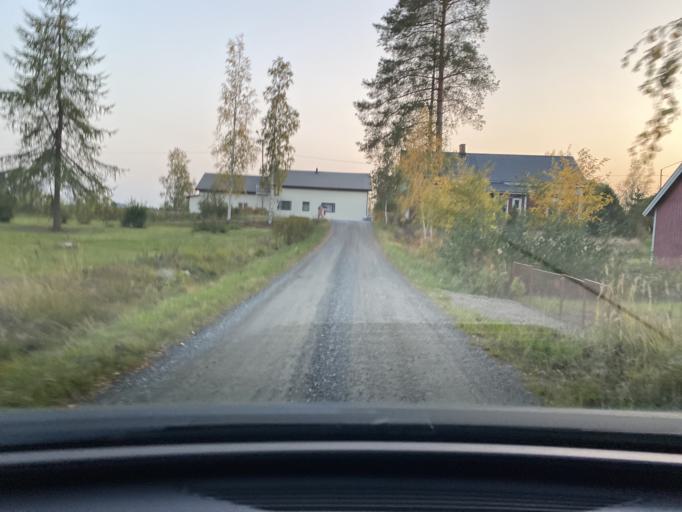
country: FI
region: Pirkanmaa
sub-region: Lounais-Pirkanmaa
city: Punkalaidun
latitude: 61.1001
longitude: 23.2058
